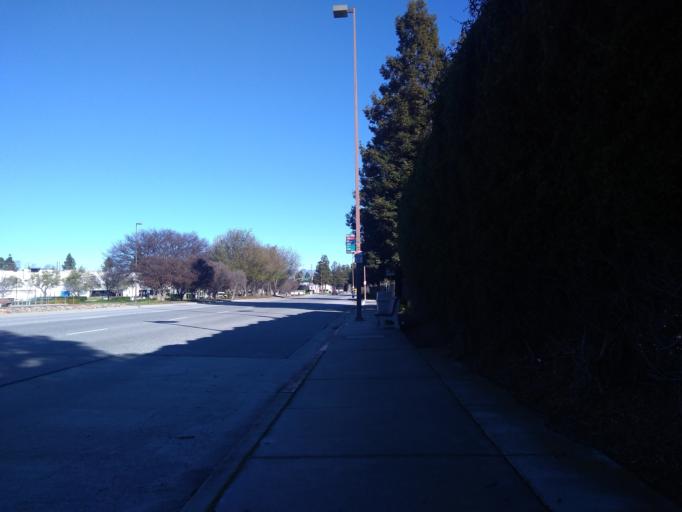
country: US
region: California
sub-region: Santa Clara County
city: Santa Clara
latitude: 37.3887
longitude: -121.9660
